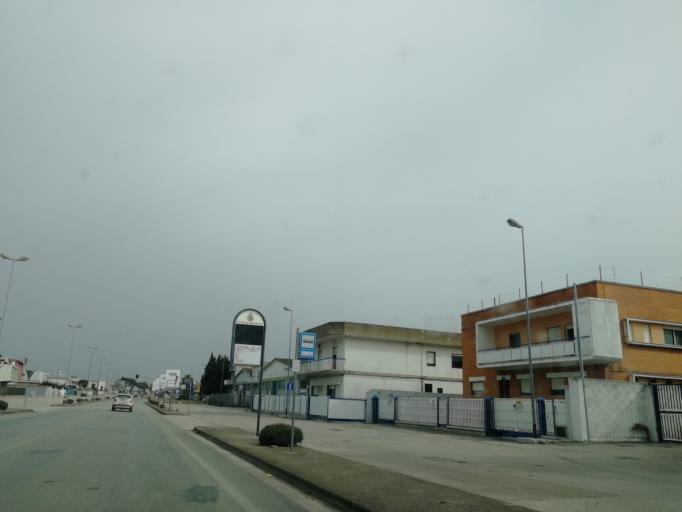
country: IT
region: Apulia
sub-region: Provincia di Barletta - Andria - Trani
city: Barletta
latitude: 41.3099
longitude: 16.3100
